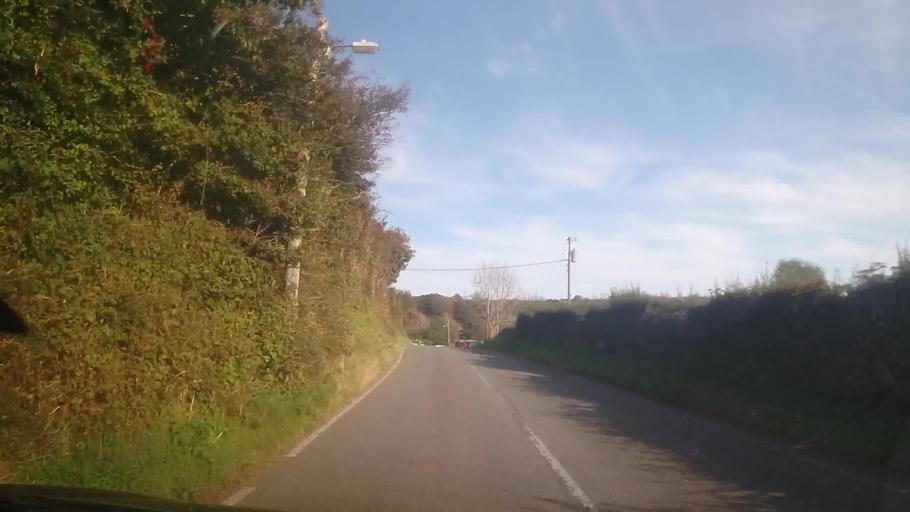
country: GB
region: Wales
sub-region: Pembrokeshire
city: Fishguard
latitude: 51.9793
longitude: -4.9288
